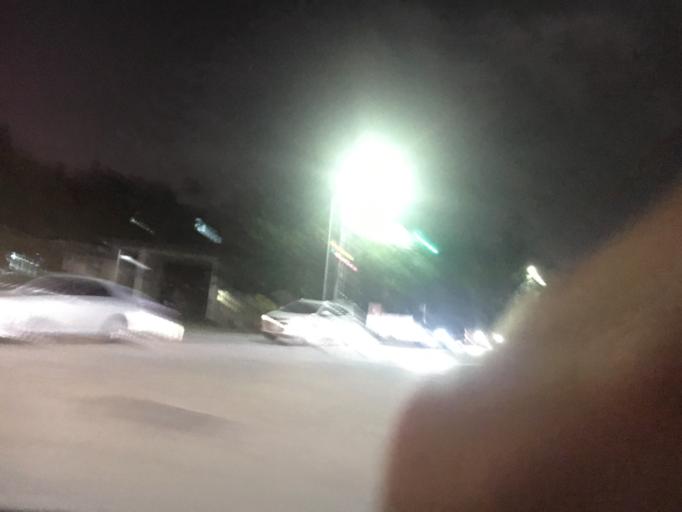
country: TW
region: Taiwan
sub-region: Hsinchu
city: Hsinchu
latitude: 24.7974
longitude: 120.9855
